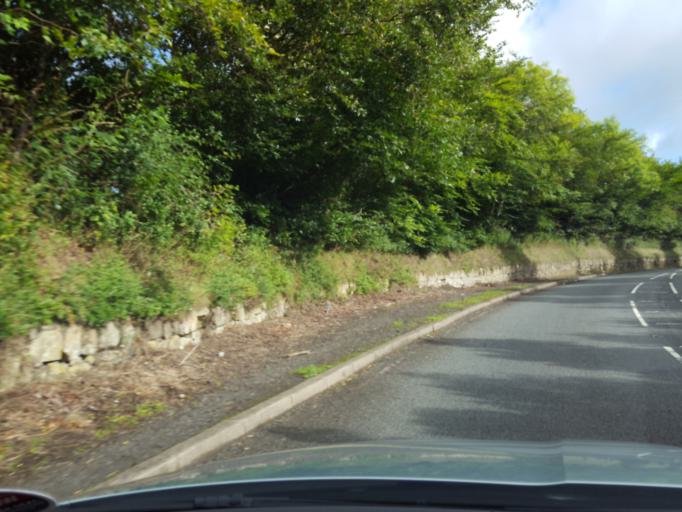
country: GB
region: Scotland
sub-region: West Lothian
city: Linlithgow
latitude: 55.9932
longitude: -3.6130
